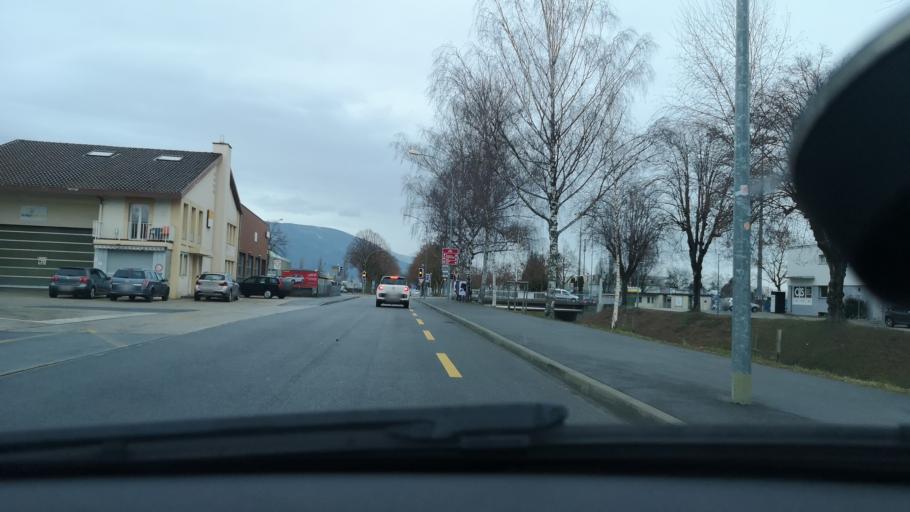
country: CH
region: Vaud
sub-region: Jura-Nord vaudois District
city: Yverdon-les-Bains
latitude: 46.7823
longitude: 6.6448
